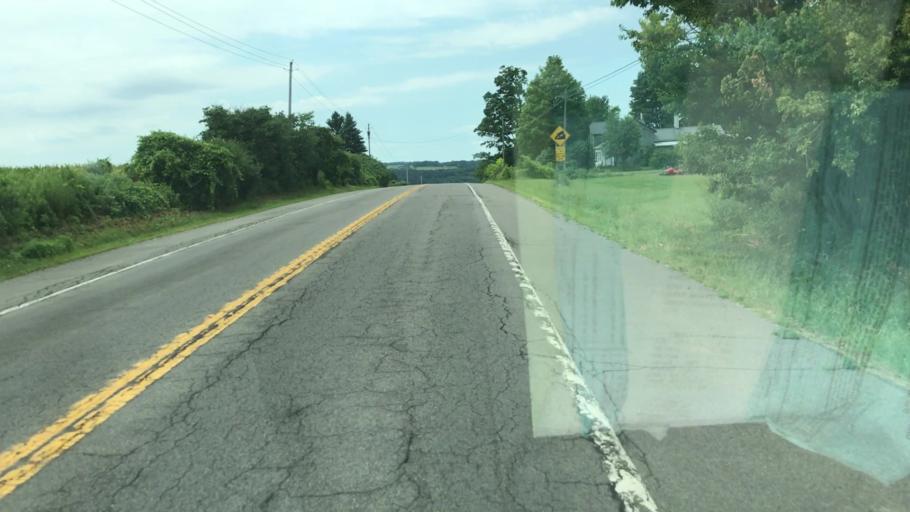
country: US
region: New York
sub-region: Onondaga County
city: Marcellus
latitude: 42.9335
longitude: -76.3092
